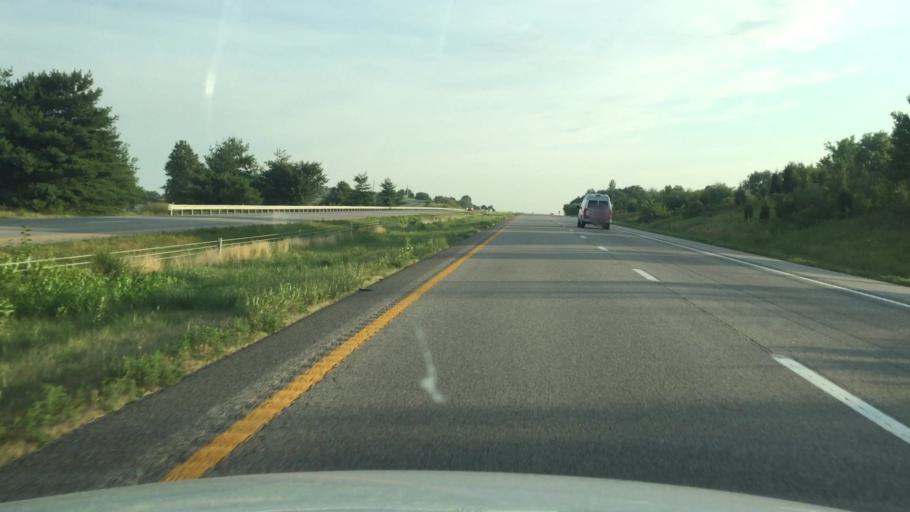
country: US
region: Missouri
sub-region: Clinton County
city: Gower
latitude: 39.5830
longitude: -94.7887
